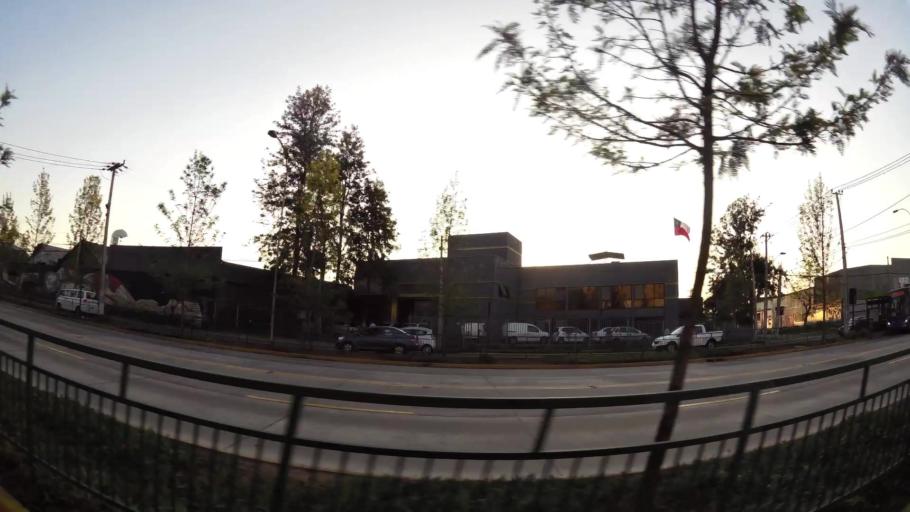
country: CL
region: Santiago Metropolitan
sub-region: Provincia de Santiago
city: Santiago
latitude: -33.4987
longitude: -70.6394
